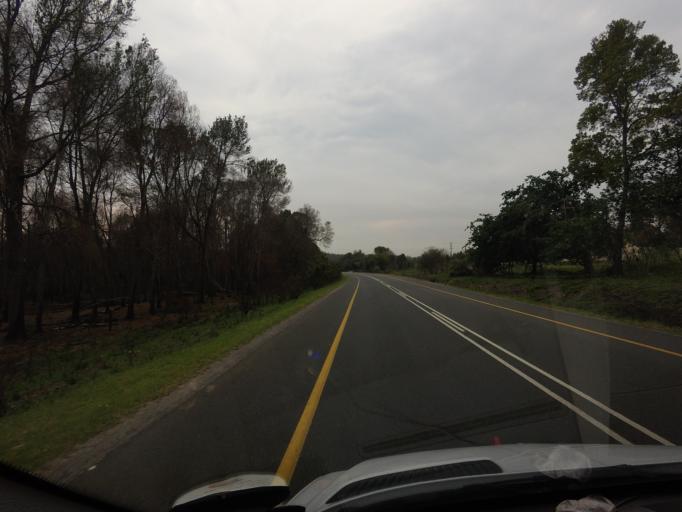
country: ZA
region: Western Cape
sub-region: Eden District Municipality
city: Knysna
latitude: -34.0373
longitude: 23.1350
